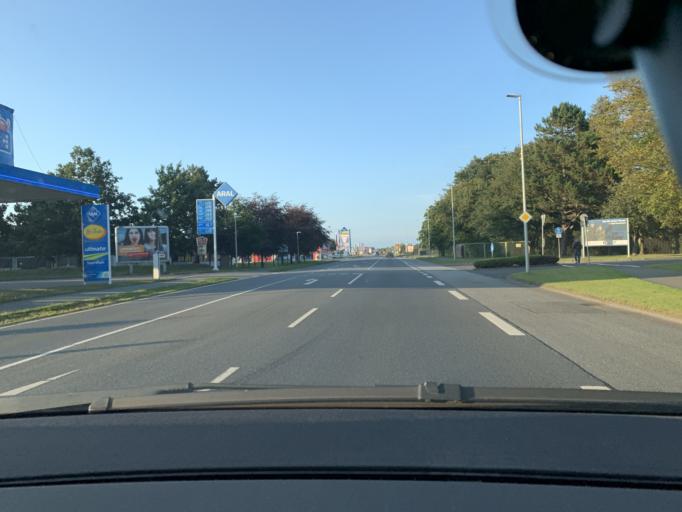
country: DE
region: Schleswig-Holstein
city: Husum
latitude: 54.4873
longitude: 9.0775
